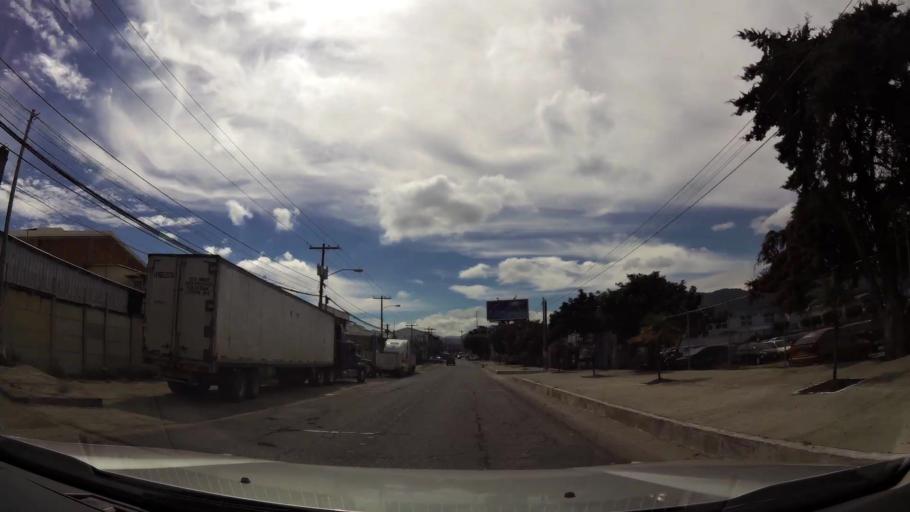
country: GT
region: Guatemala
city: Mixco
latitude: 14.6406
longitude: -90.5843
